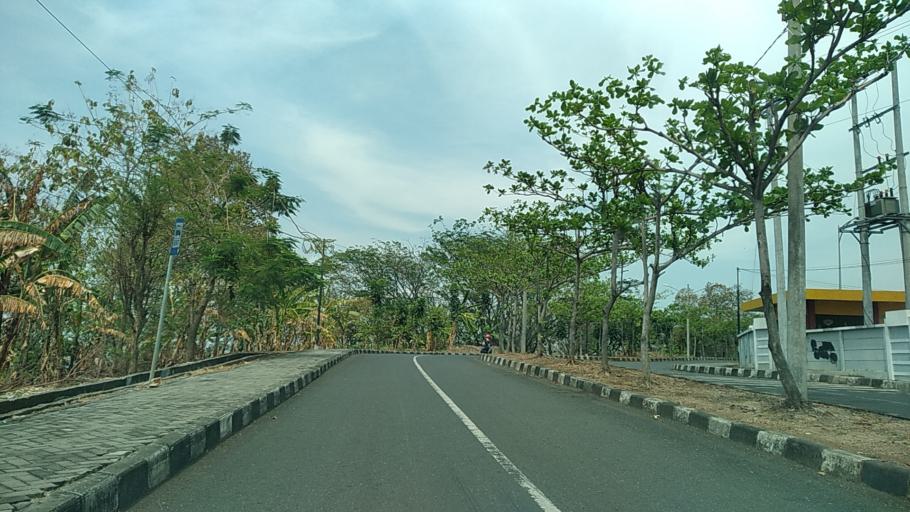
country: ID
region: Central Java
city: Semarang
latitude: -7.0461
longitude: 110.4416
